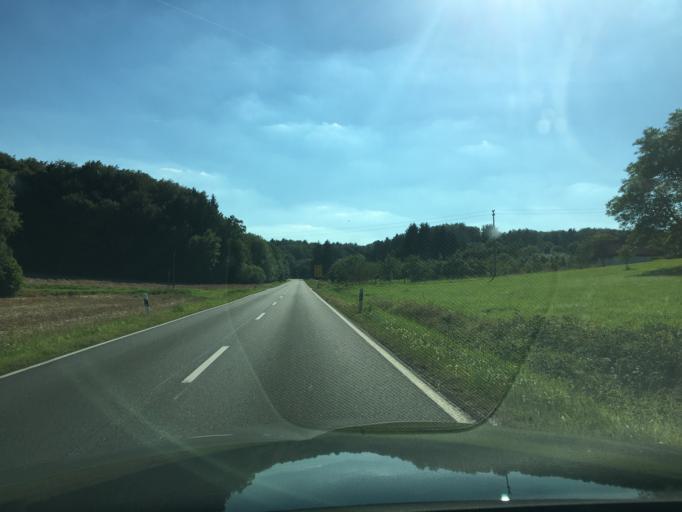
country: DE
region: Bavaria
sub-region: Upper Franconia
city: Obertrubach
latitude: 49.6718
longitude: 11.3533
